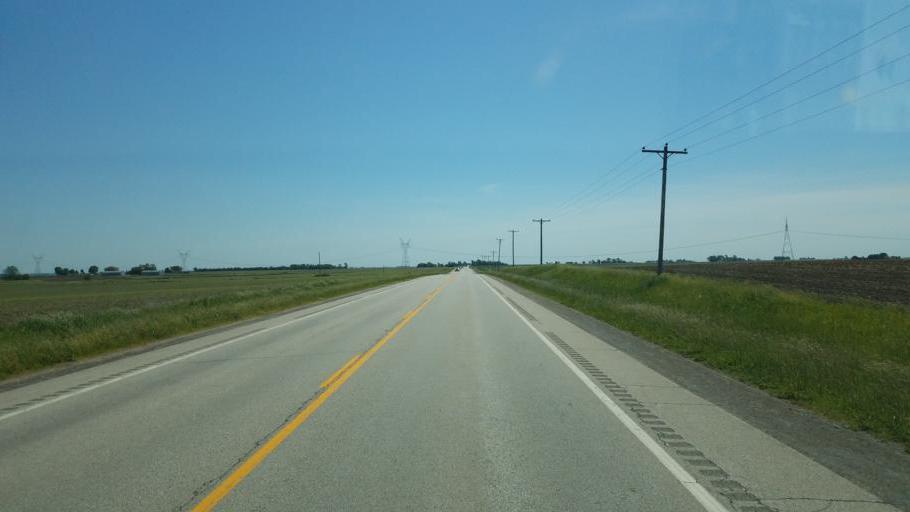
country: US
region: Illinois
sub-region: McLean County
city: Heyworth
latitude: 40.3123
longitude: -88.9420
